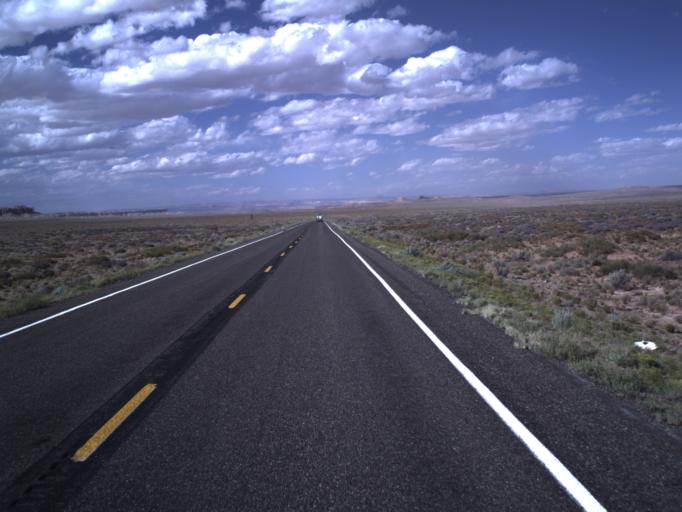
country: US
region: Utah
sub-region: Wayne County
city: Loa
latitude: 38.1658
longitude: -110.6231
